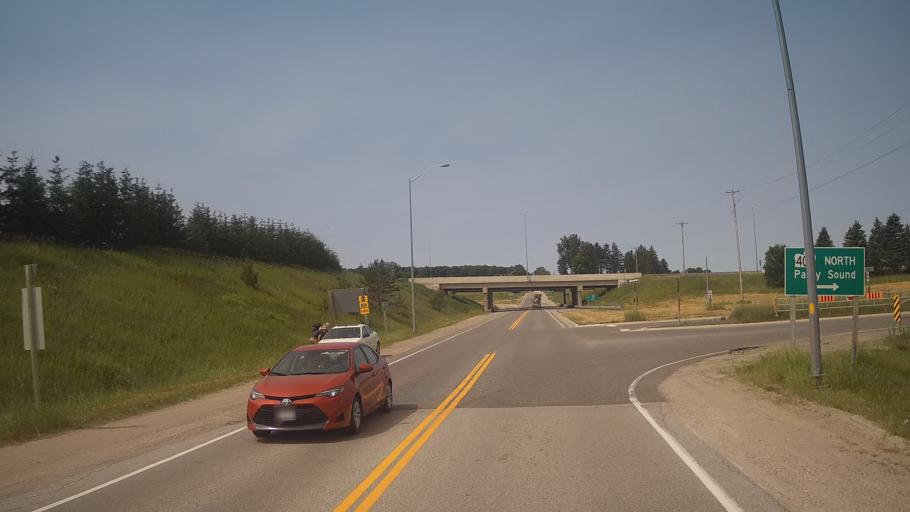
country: CA
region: Ontario
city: Barrie
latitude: 44.4777
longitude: -79.6936
